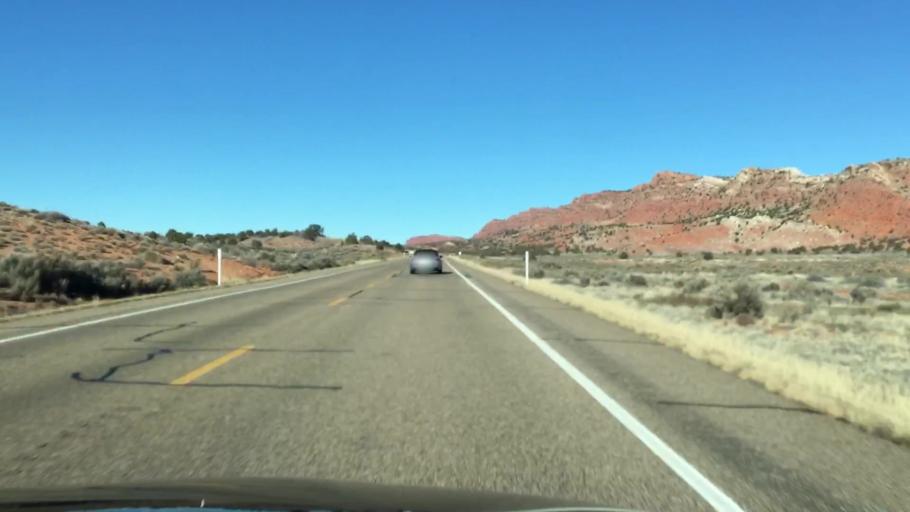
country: US
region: Utah
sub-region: Kane County
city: Kanab
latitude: 37.1497
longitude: -111.9710
